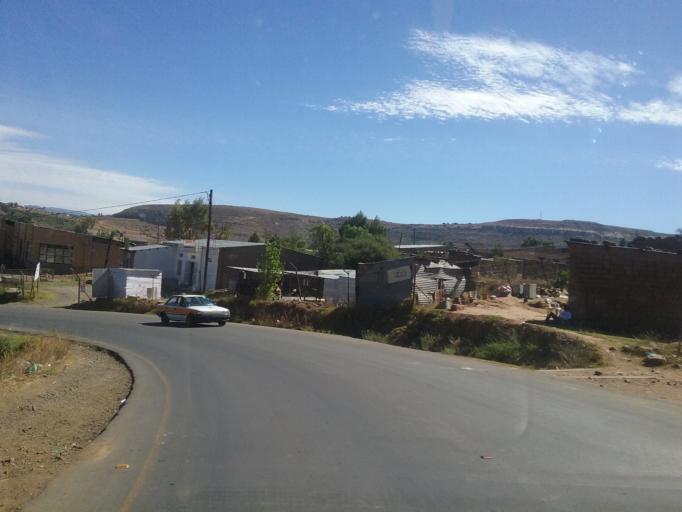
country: LS
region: Quthing
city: Quthing
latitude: -30.4012
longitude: 27.7046
